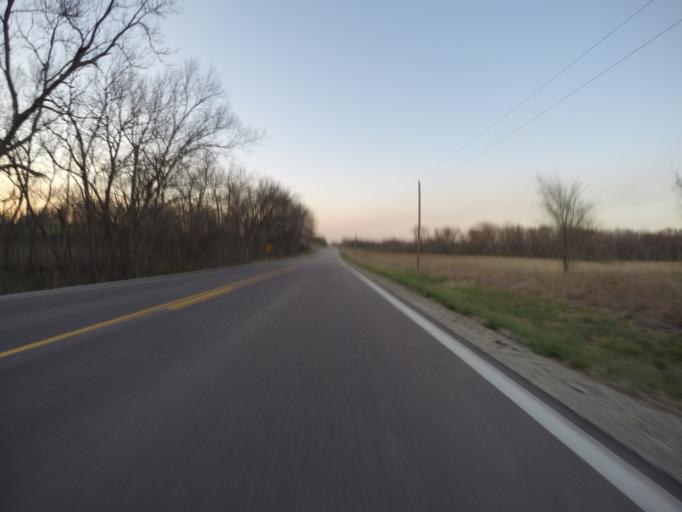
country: US
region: Kansas
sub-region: Riley County
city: Ogden
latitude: 39.0791
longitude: -96.6561
